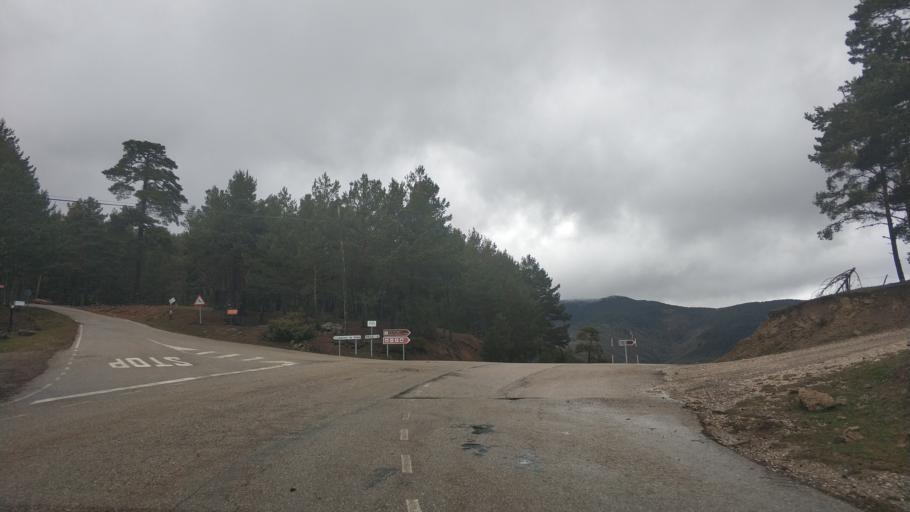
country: ES
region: Castille and Leon
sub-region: Provincia de Burgos
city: Neila
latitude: 42.0425
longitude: -3.0102
